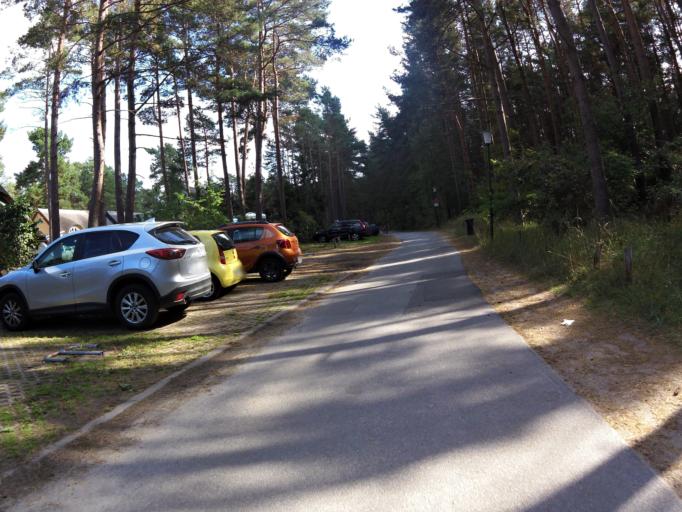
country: DE
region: Mecklenburg-Vorpommern
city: Karlshagen
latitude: 54.1132
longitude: 13.8509
